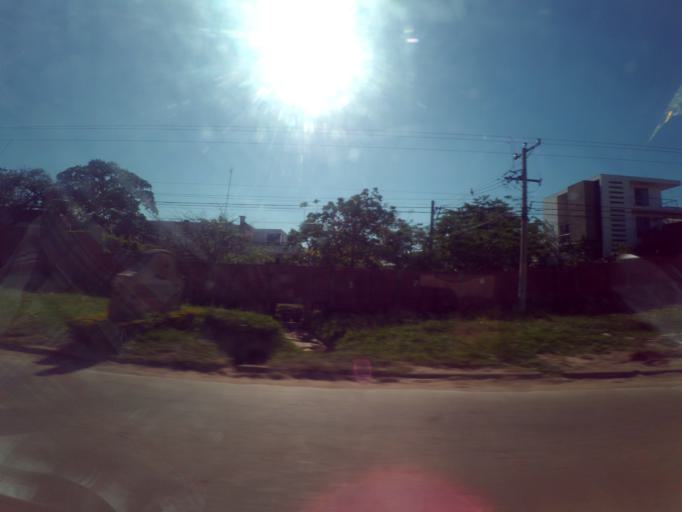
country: BO
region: Santa Cruz
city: Santa Cruz de la Sierra
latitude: -17.7608
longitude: -63.2220
